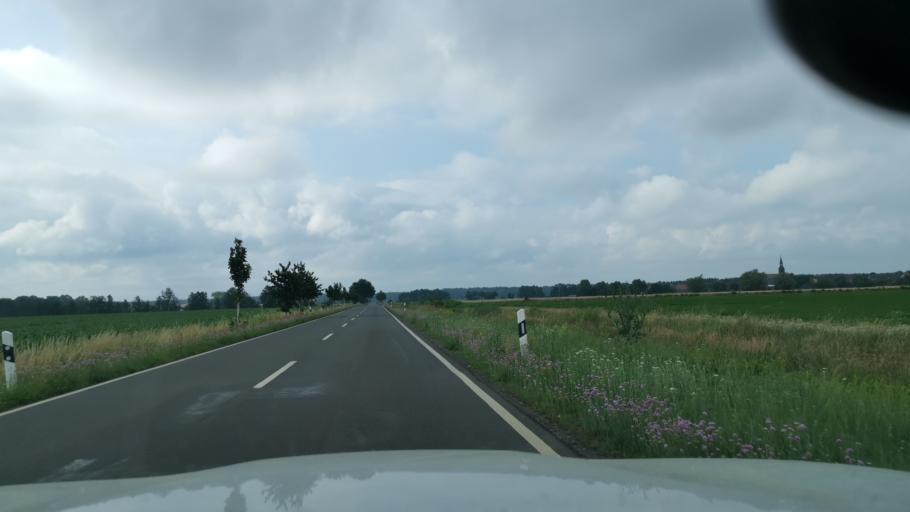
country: DE
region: Saxony-Anhalt
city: Annaburg
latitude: 51.7703
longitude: 13.0280
